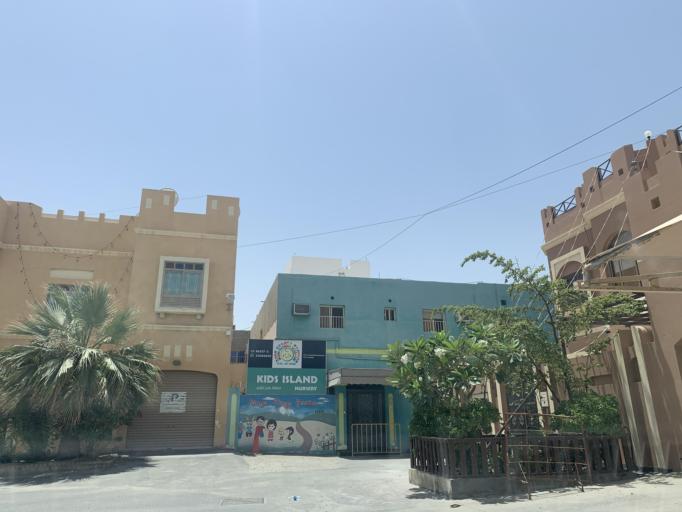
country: BH
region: Northern
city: Sitrah
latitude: 26.1627
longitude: 50.6230
